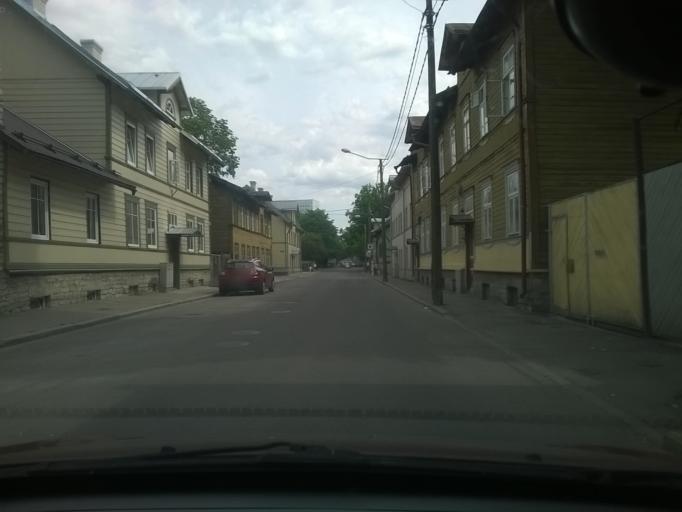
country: EE
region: Harju
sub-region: Tallinna linn
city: Tallinn
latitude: 59.4253
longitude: 24.7313
